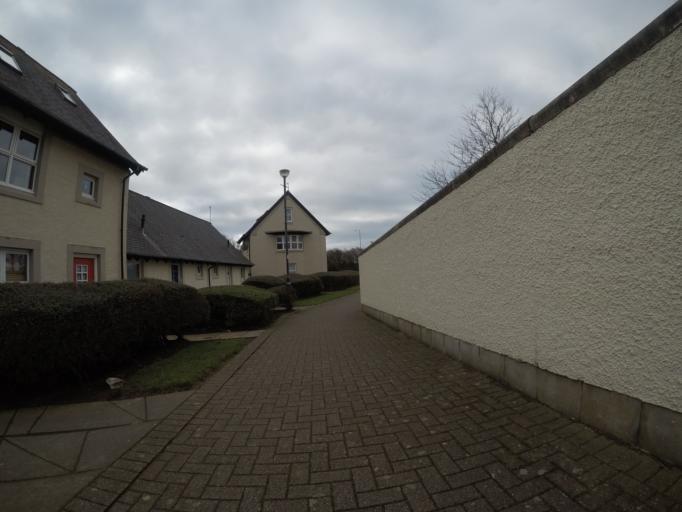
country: GB
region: Scotland
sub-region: North Ayrshire
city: Irvine
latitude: 55.6075
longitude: -4.6812
